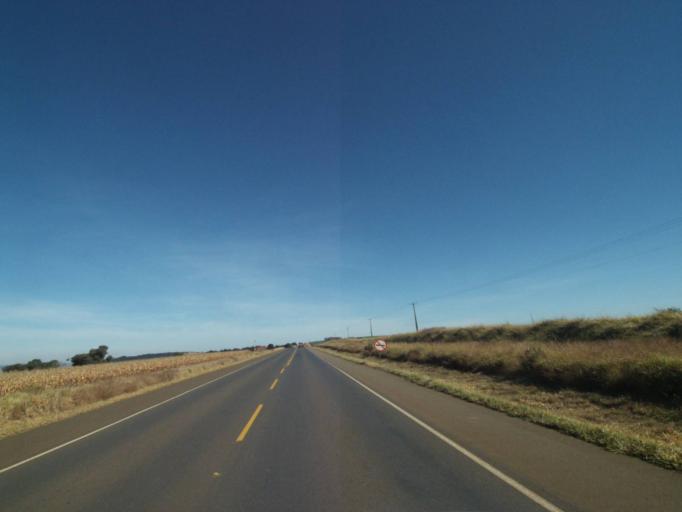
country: BR
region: Parana
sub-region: Tibagi
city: Tibagi
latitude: -24.3541
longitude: -50.3158
